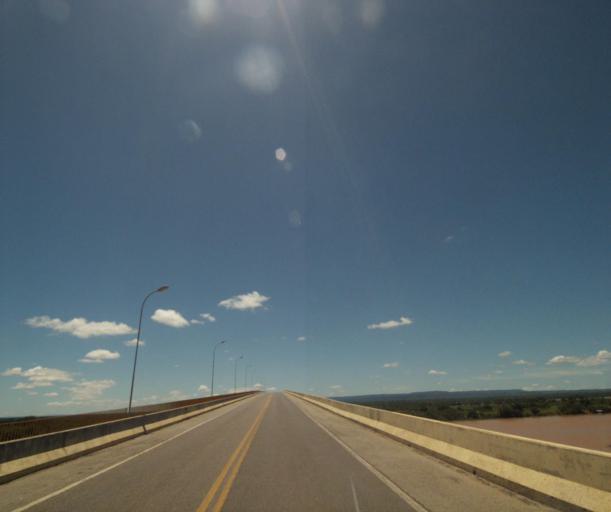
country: BR
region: Bahia
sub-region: Carinhanha
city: Carinhanha
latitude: -14.3244
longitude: -43.7707
